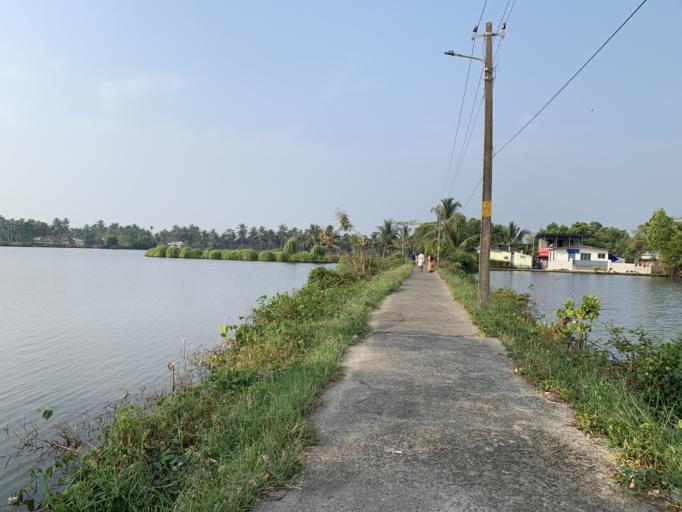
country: IN
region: Kerala
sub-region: Ernakulam
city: Elur
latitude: 10.0183
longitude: 76.2211
